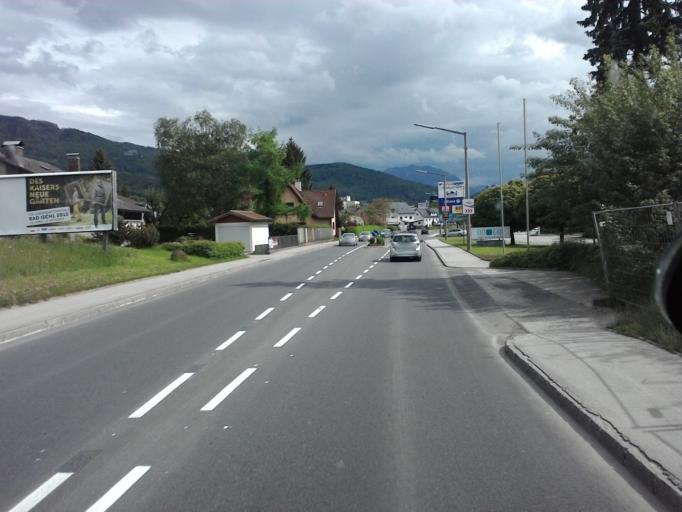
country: AT
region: Upper Austria
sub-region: Politischer Bezirk Kirchdorf an der Krems
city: Micheldorf in Oberoesterreich
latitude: 47.9013
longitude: 14.1255
